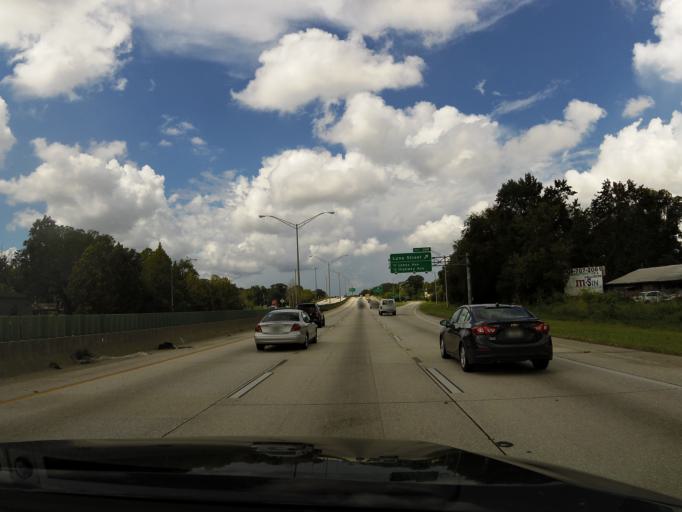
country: US
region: Florida
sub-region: Duval County
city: Jacksonville
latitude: 30.3211
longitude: -81.7158
